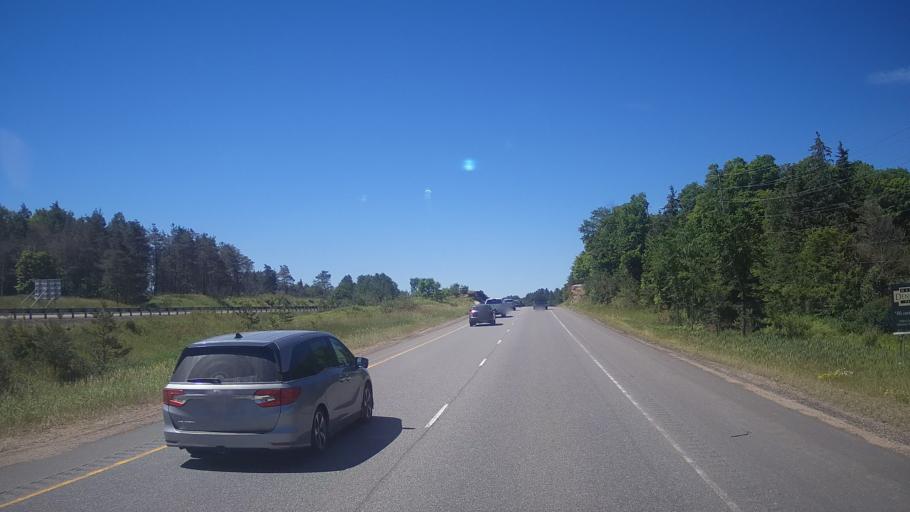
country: CA
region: Ontario
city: Huntsville
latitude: 45.2691
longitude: -79.2873
